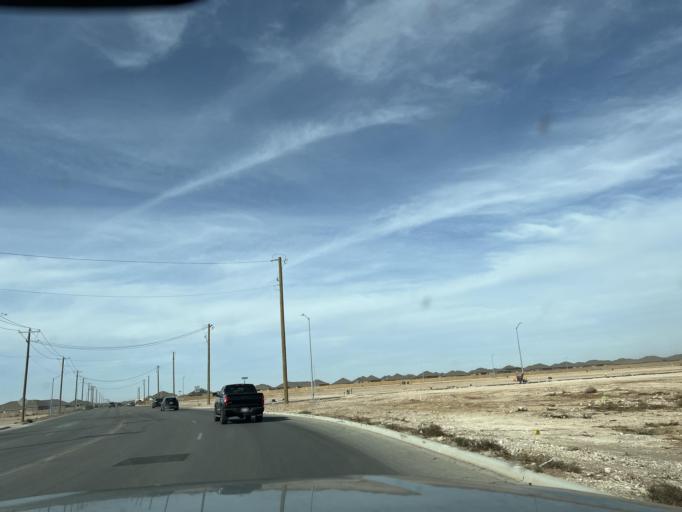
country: US
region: Texas
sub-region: Ector County
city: Gardendale
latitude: 31.9390
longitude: -102.3825
